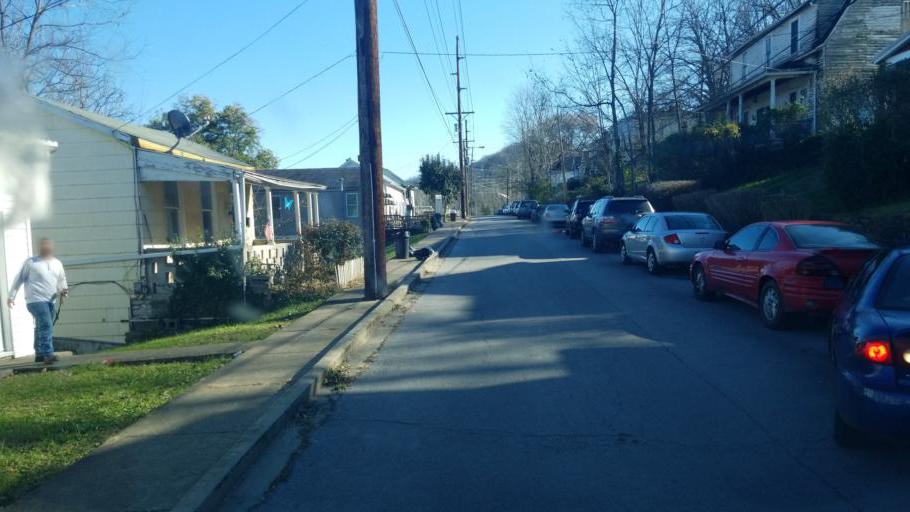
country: US
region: Ohio
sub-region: Brown County
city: Aberdeen
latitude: 38.6421
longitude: -83.7591
